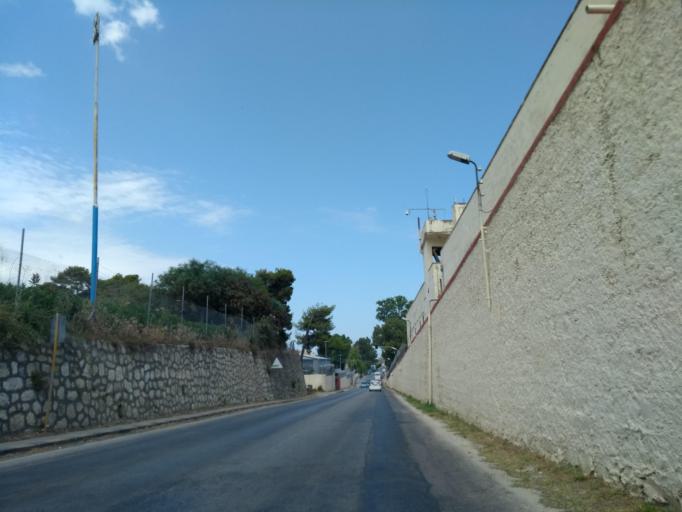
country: GR
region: Crete
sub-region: Nomos Chanias
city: Souda
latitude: 35.4866
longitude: 24.0804
